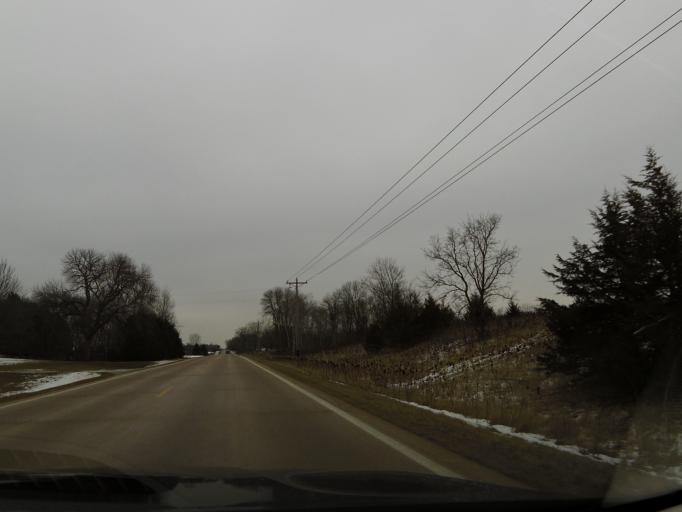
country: US
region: Minnesota
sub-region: Carver County
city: Carver
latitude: 44.7180
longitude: -93.6679
